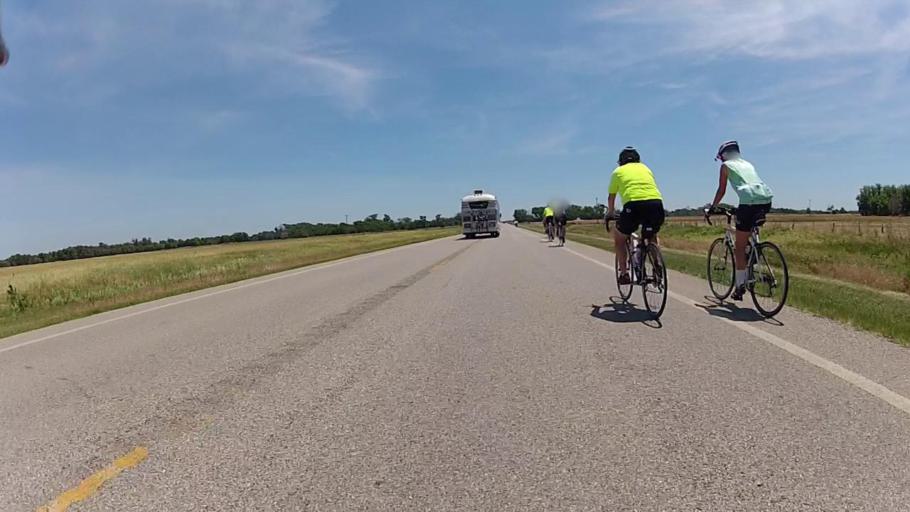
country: US
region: Kansas
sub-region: Barber County
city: Medicine Lodge
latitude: 37.2534
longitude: -98.4618
